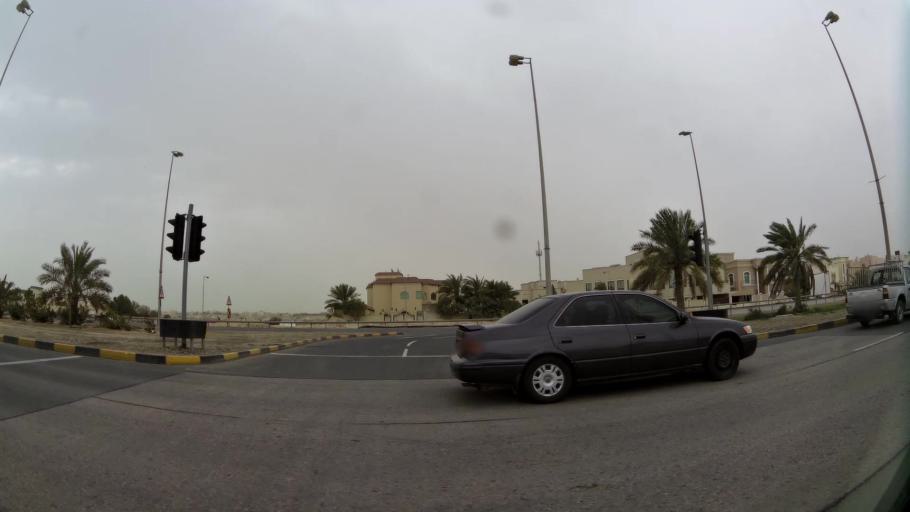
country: BH
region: Northern
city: Madinat `Isa
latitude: 26.1581
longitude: 50.5555
